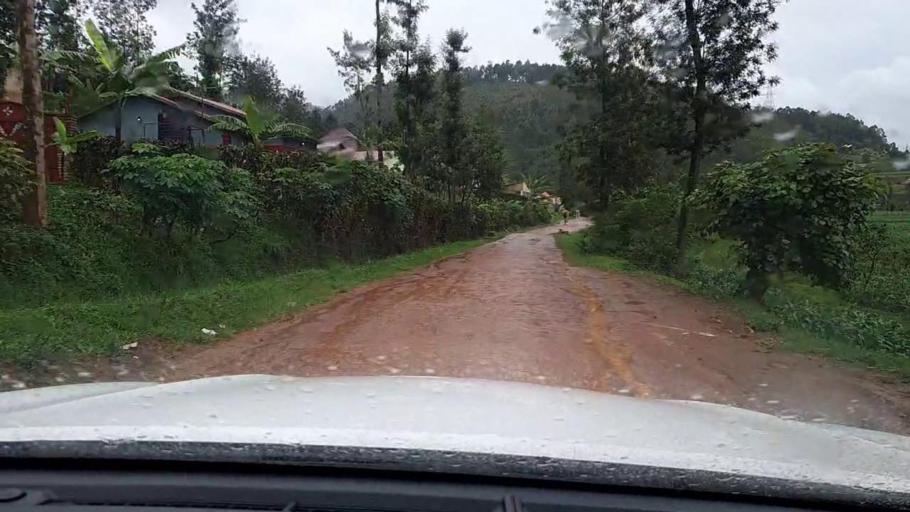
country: RW
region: Northern Province
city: Byumba
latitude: -1.7251
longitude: 29.9320
